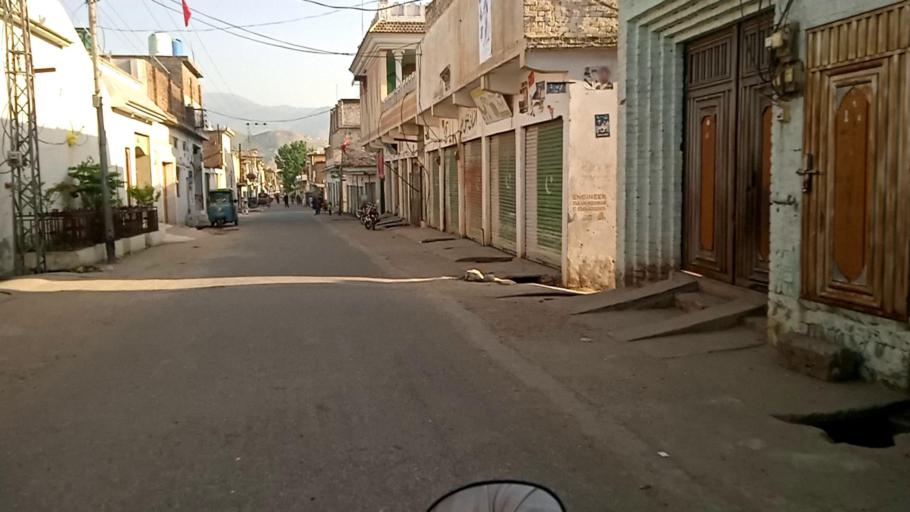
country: PK
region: Khyber Pakhtunkhwa
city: Mingora
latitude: 34.8136
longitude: 72.3593
